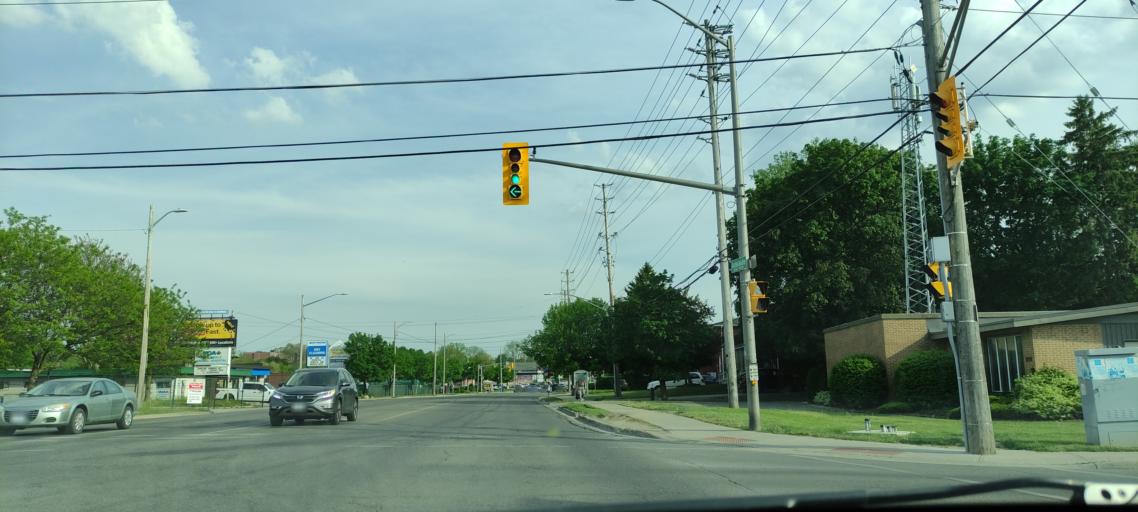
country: CA
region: Ontario
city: London
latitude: 43.0118
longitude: -81.2432
